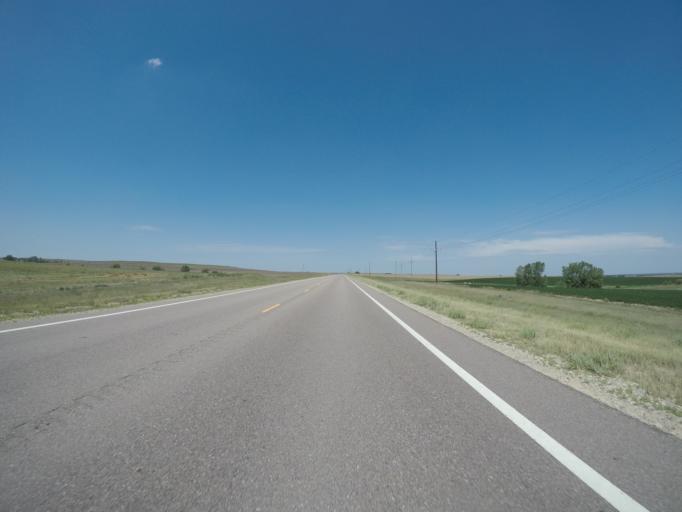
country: US
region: Kansas
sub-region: Osborne County
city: Osborne
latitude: 39.5100
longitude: -98.6710
